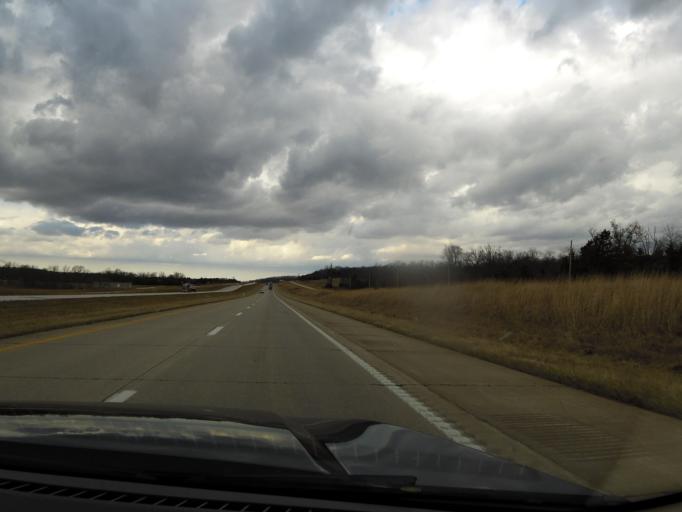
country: US
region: Missouri
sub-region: Pike County
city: Bowling Green
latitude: 39.4504
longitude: -91.2688
